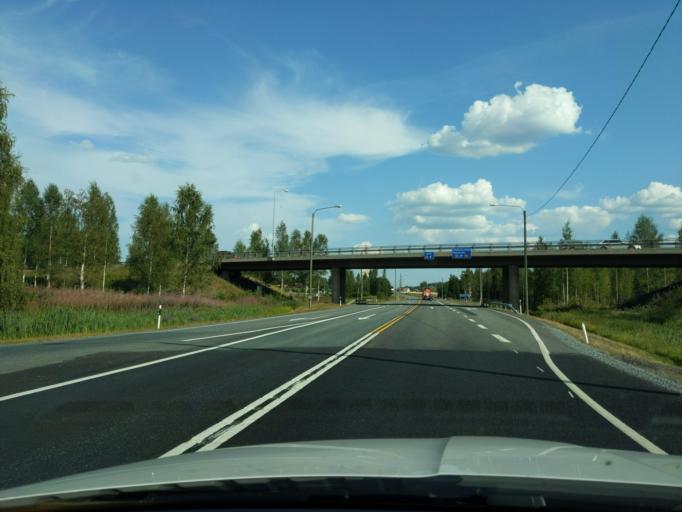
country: FI
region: Haeme
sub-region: Haemeenlinna
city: Tuulos
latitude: 61.1056
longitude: 24.8575
